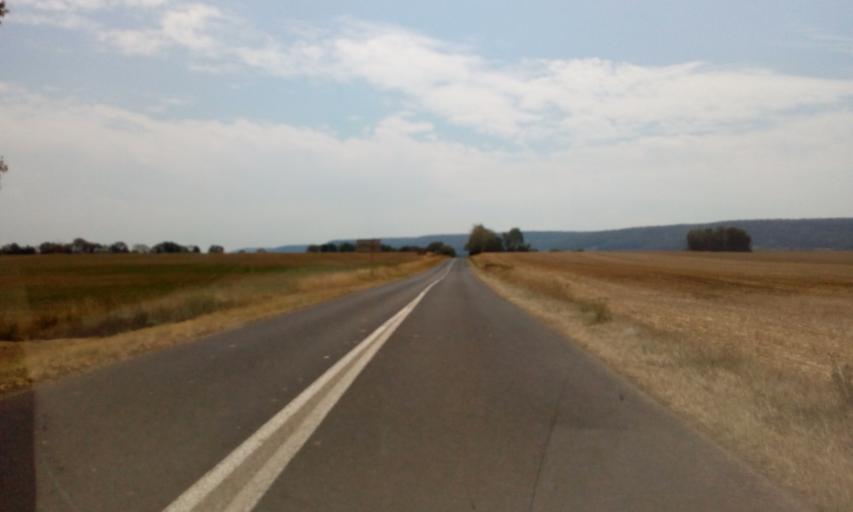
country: FR
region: Lorraine
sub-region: Departement de la Meuse
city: Vigneulles-les-Hattonchatel
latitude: 49.0677
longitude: 5.6463
